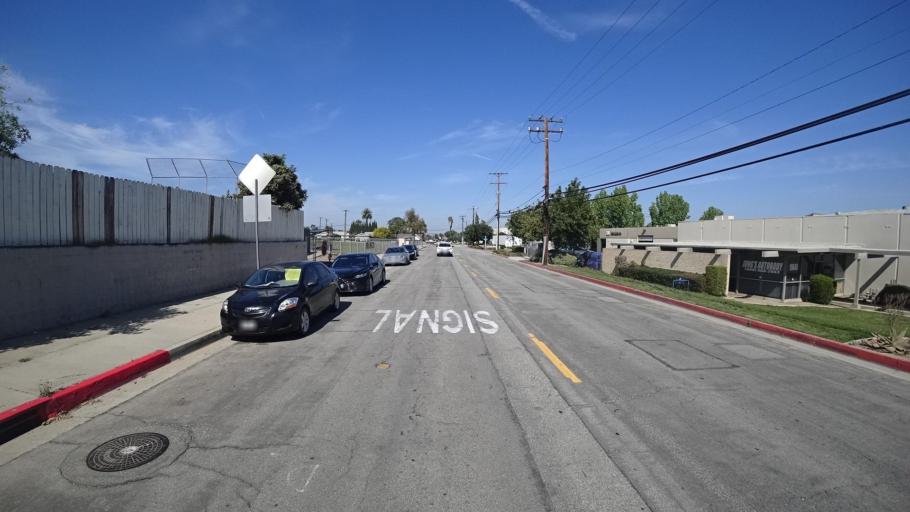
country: US
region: California
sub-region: Los Angeles County
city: Walnut
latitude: 33.9930
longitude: -117.8713
